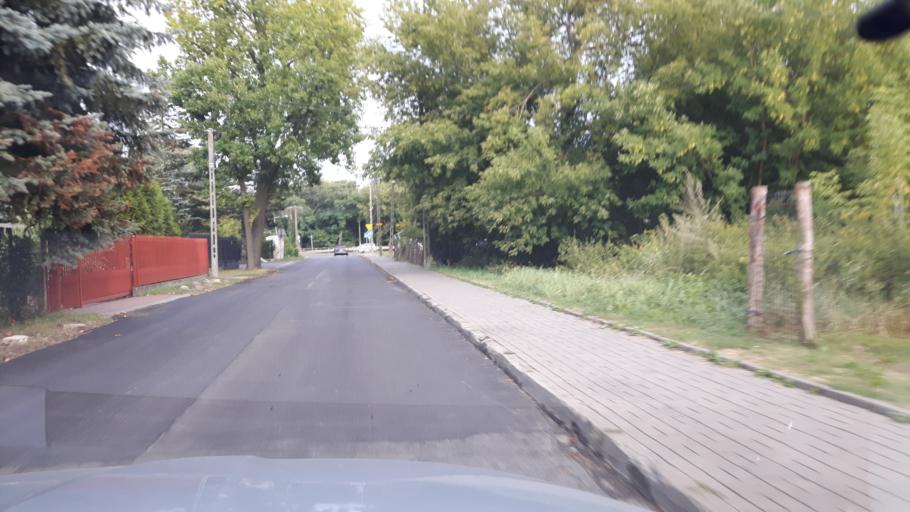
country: PL
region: Masovian Voivodeship
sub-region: Powiat wolominski
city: Marki
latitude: 52.3276
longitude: 21.1070
